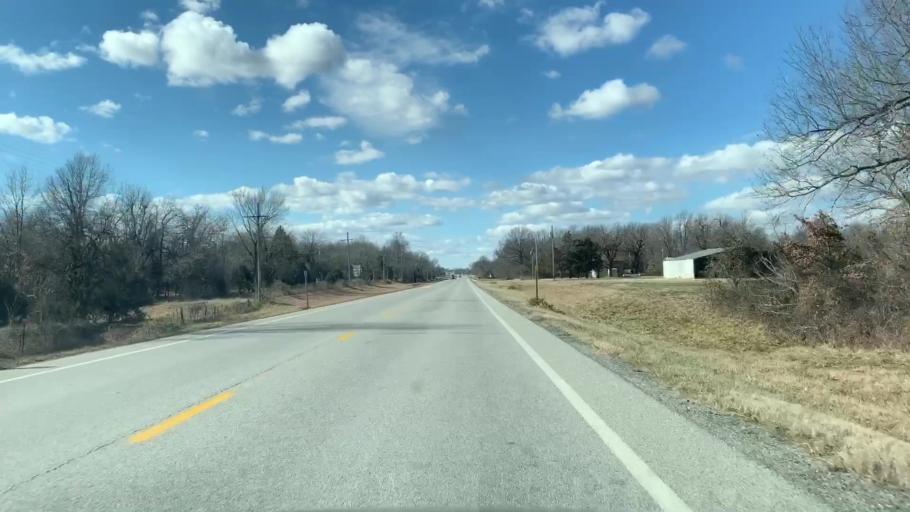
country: US
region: Kansas
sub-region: Cherokee County
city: Columbus
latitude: 37.1781
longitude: -94.8162
